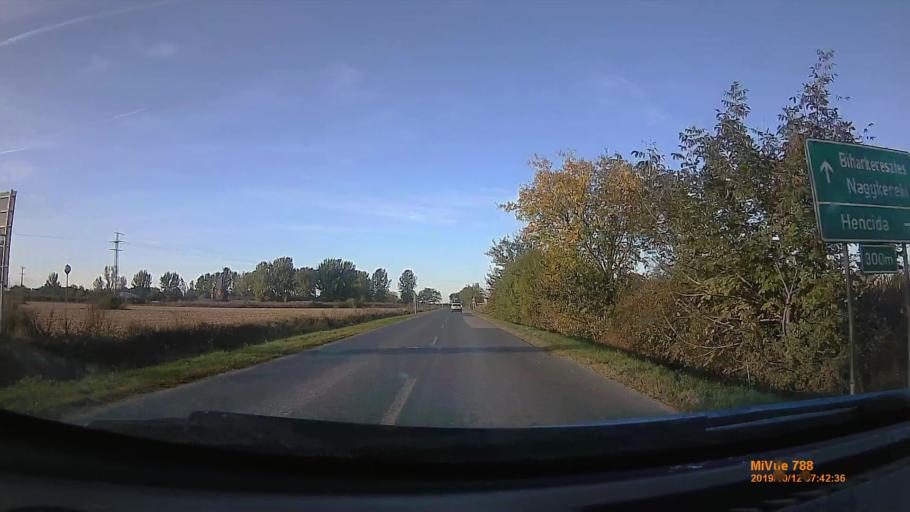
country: HU
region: Hajdu-Bihar
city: Pocsaj
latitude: 47.2005
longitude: 21.7917
